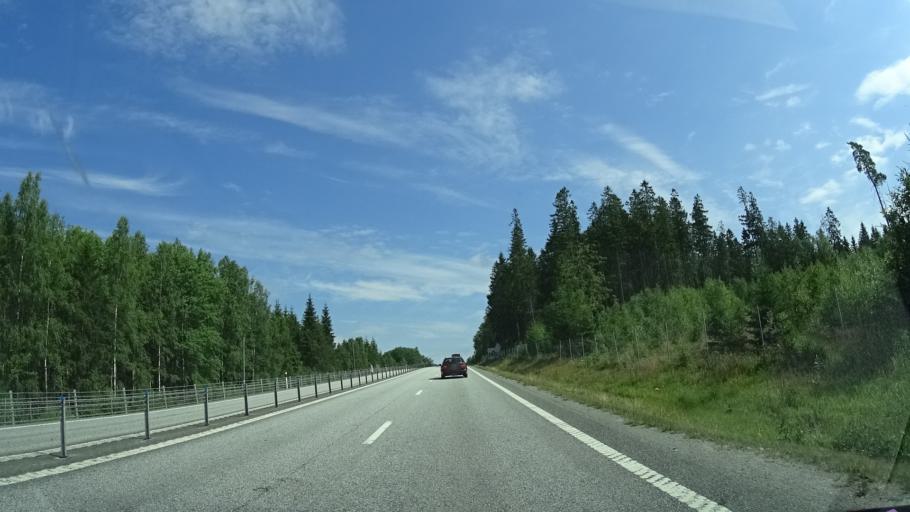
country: SE
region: Vaermland
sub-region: Kristinehamns Kommun
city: Bjorneborg
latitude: 59.3163
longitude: 14.3340
